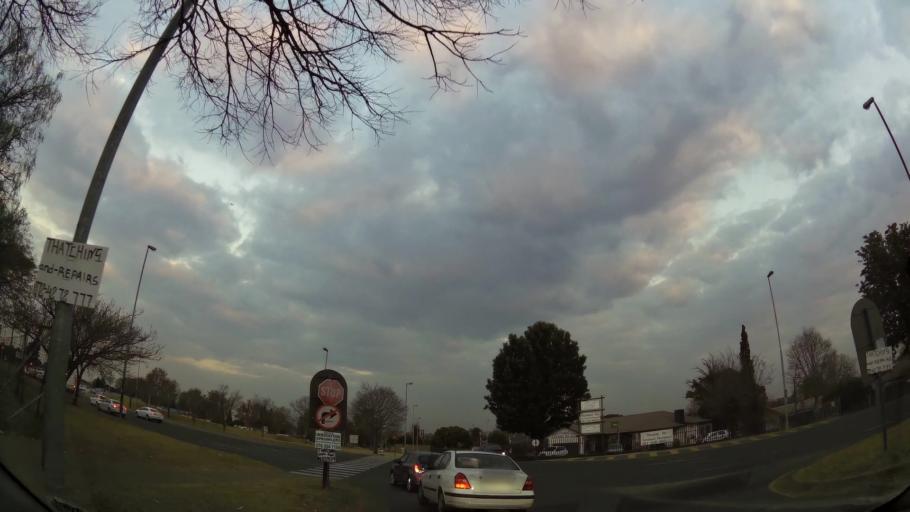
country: ZA
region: Gauteng
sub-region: Ekurhuleni Metropolitan Municipality
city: Benoni
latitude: -26.1776
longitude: 28.3096
